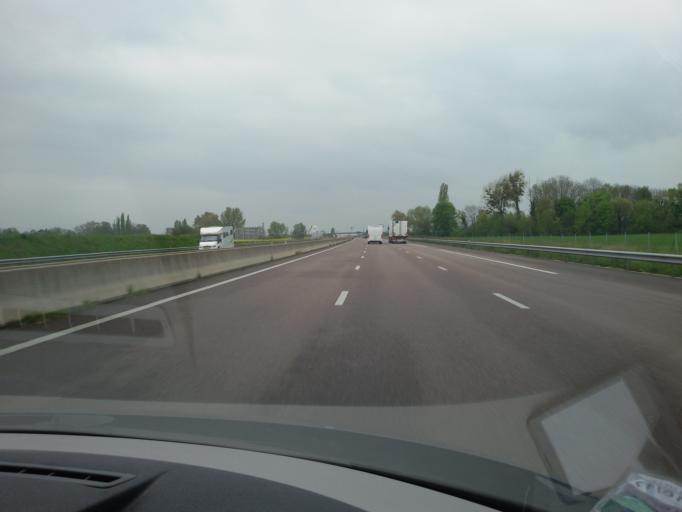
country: FR
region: Bourgogne
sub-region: Departement de la Cote-d'Or
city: Nuits-Saint-Georges
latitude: 47.1134
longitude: 4.9610
